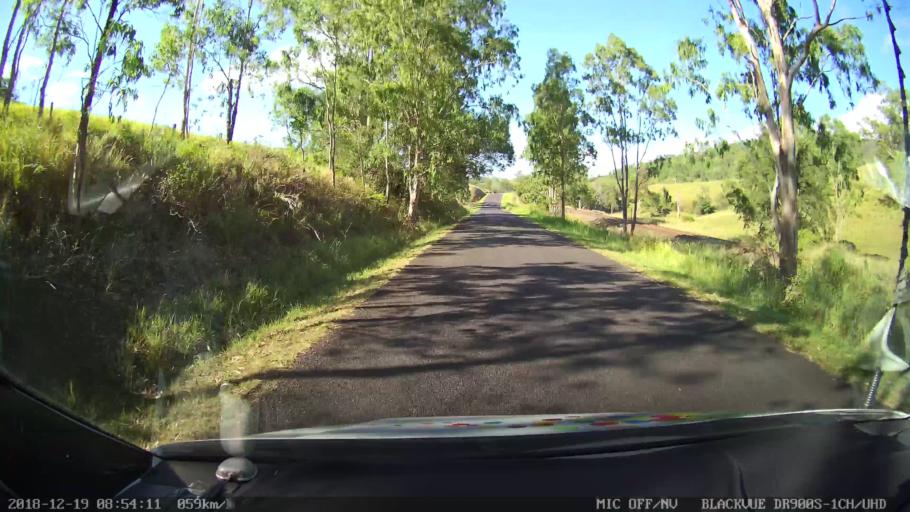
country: AU
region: New South Wales
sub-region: Kyogle
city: Kyogle
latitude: -28.4082
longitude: 152.9796
